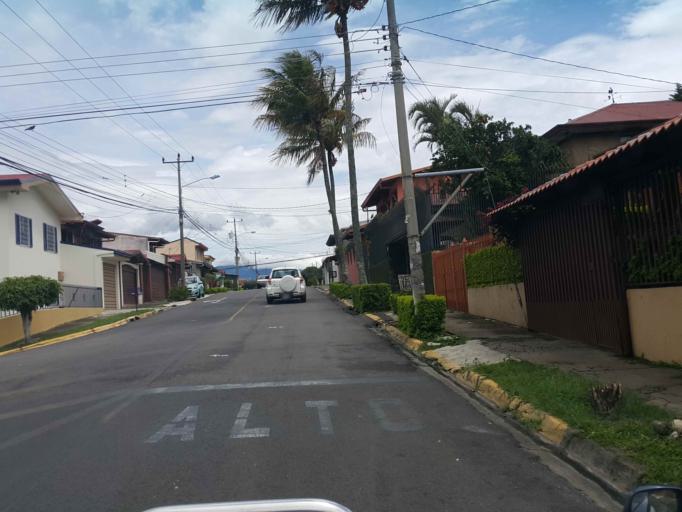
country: CR
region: Heredia
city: Heredia
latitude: 10.0161
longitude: -84.1175
